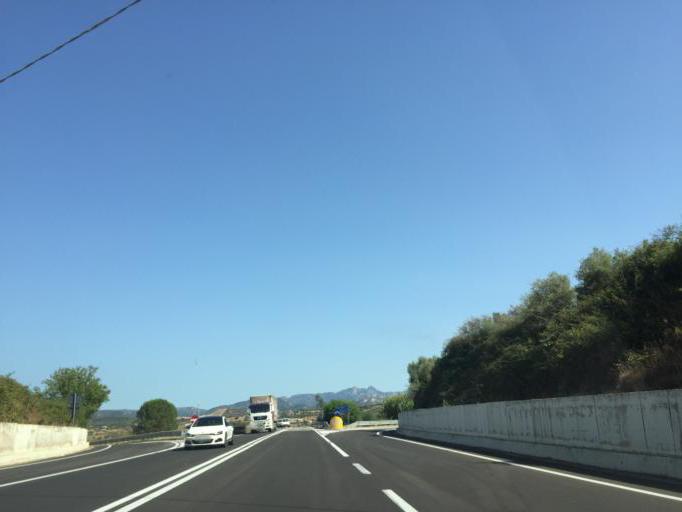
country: IT
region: Sardinia
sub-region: Provincia di Olbia-Tempio
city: Olbia
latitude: 40.8961
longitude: 9.4843
